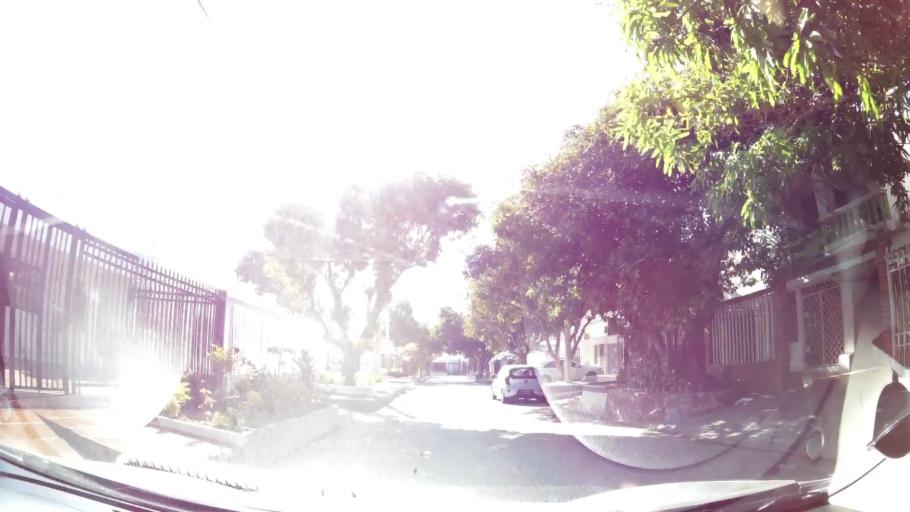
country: CO
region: Atlantico
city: Barranquilla
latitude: 11.0200
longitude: -74.8027
